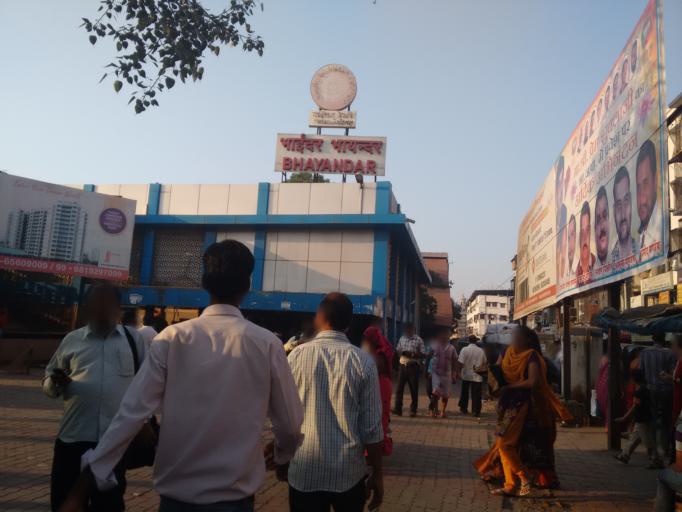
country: IN
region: Maharashtra
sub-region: Thane
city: Bhayandar
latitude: 19.3101
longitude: 72.8532
